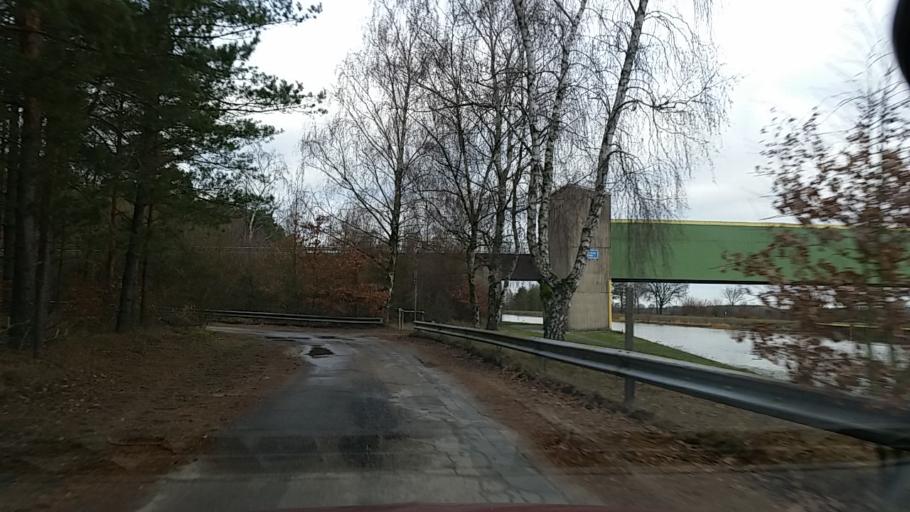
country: DE
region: Lower Saxony
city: Wieren
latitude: 52.8773
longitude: 10.6425
